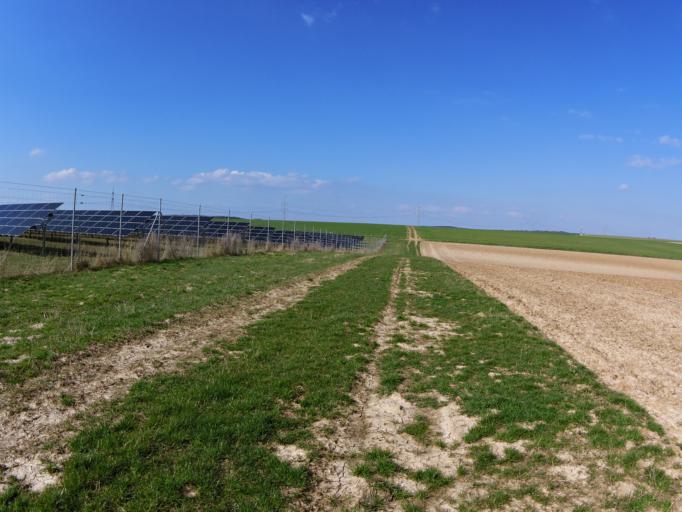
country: DE
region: Bavaria
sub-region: Regierungsbezirk Unterfranken
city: Biebelried
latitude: 49.7917
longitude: 10.0713
